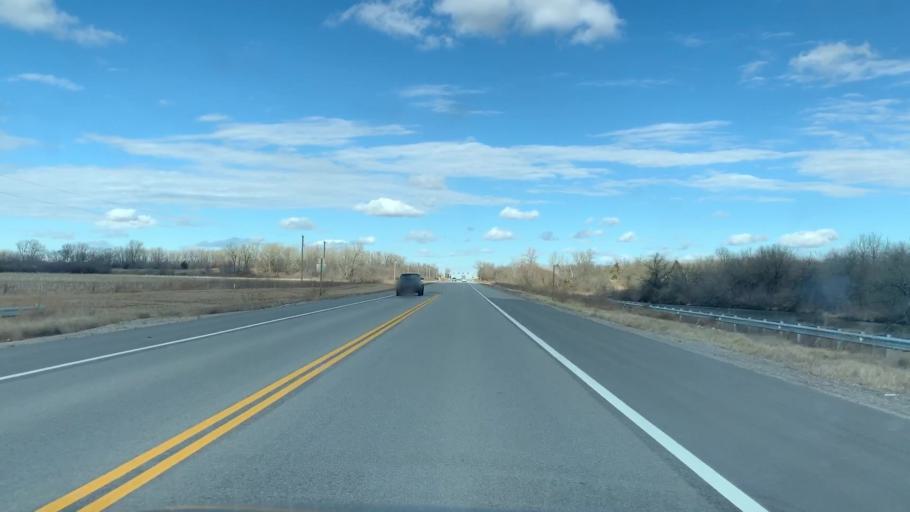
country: US
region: Kansas
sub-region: Cherokee County
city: Columbus
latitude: 37.3156
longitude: -94.8323
